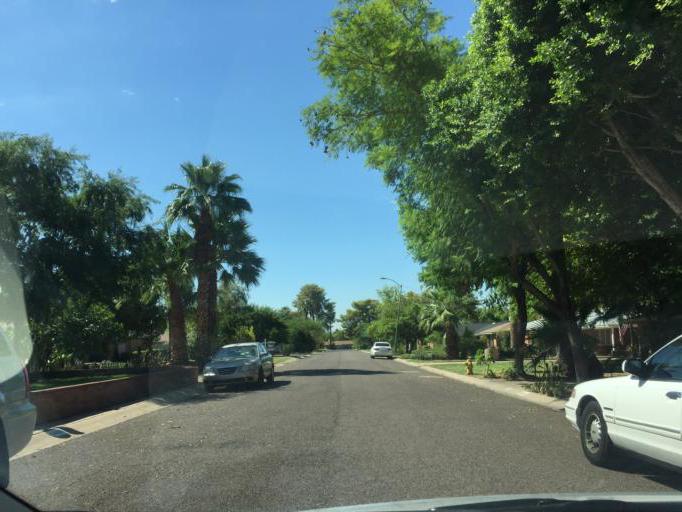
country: US
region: Arizona
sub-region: Maricopa County
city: Phoenix
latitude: 33.5368
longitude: -112.0502
